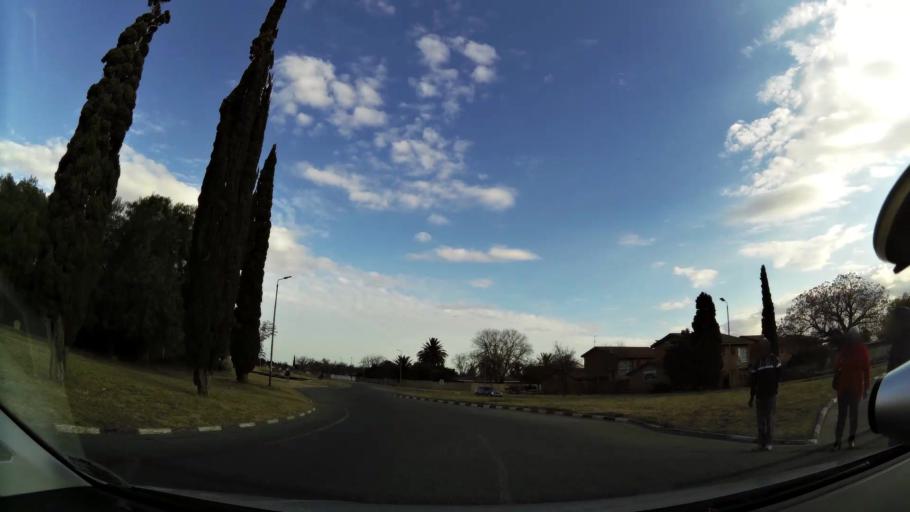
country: ZA
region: Orange Free State
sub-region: Lejweleputswa District Municipality
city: Welkom
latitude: -27.9821
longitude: 26.7120
